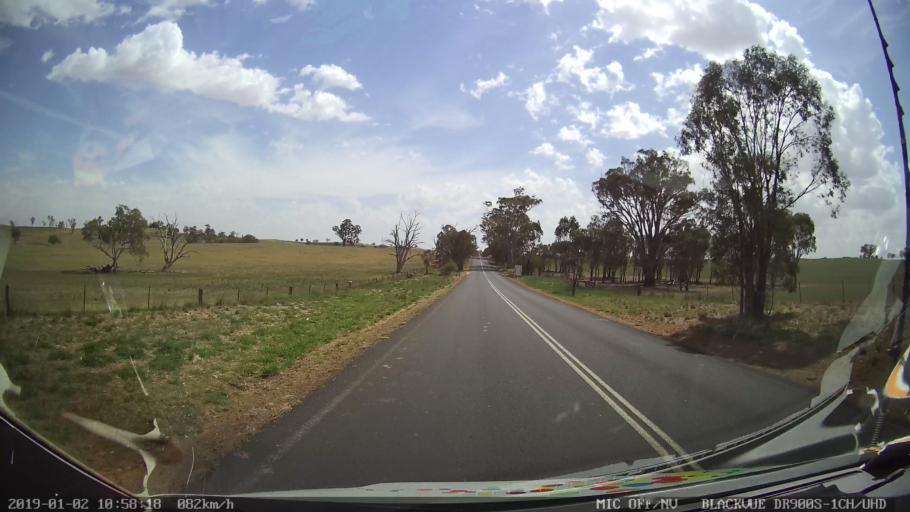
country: AU
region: New South Wales
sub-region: Cootamundra
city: Cootamundra
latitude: -34.6260
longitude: 148.2900
